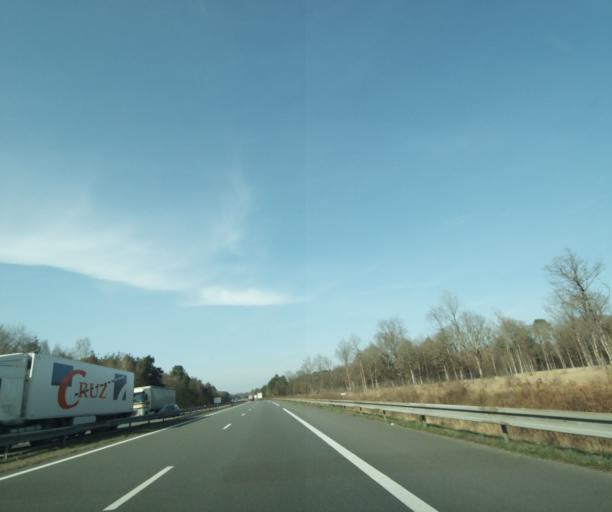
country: FR
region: Centre
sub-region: Departement du Loir-et-Cher
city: Nouan-le-Fuzelier
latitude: 47.4812
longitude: 2.0091
